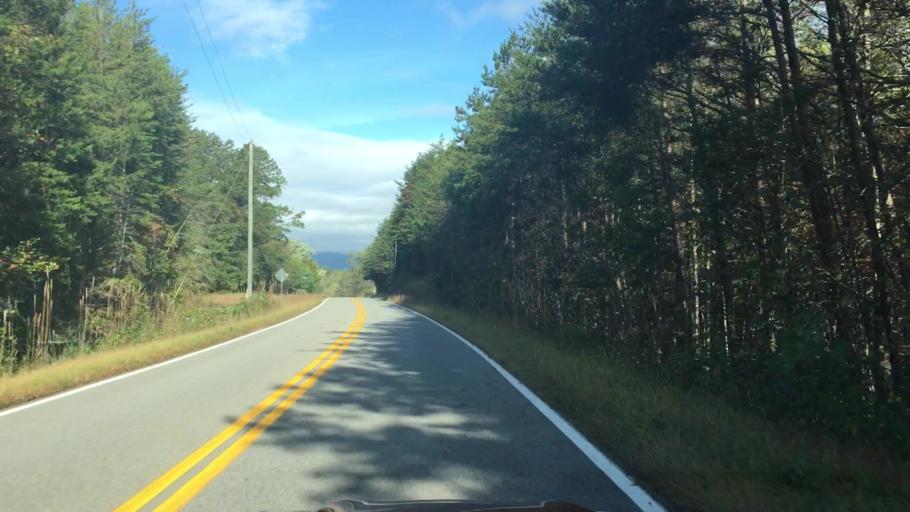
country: US
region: Georgia
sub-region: Lumpkin County
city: Dahlonega
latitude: 34.5907
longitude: -83.8874
